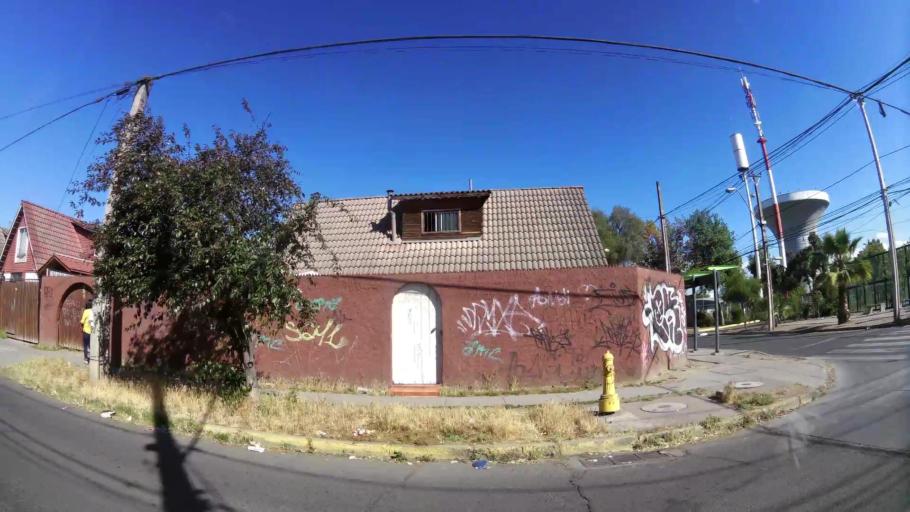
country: CL
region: Santiago Metropolitan
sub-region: Provincia de Maipo
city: San Bernardo
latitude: -33.5637
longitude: -70.7828
